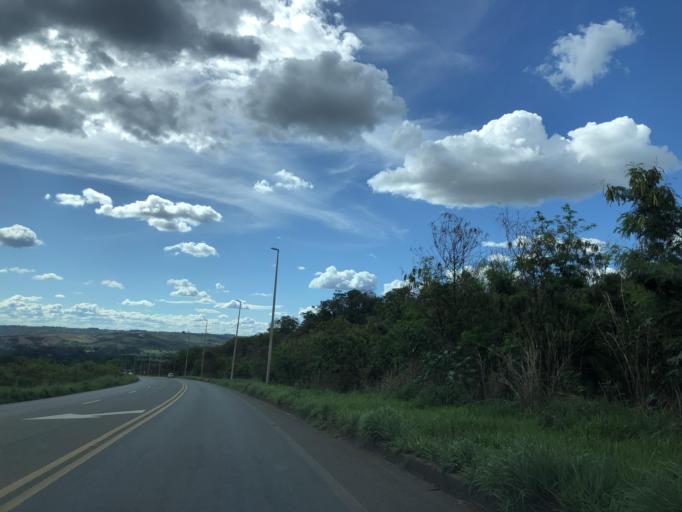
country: BR
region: Goias
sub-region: Luziania
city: Luziania
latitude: -16.0245
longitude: -48.0895
